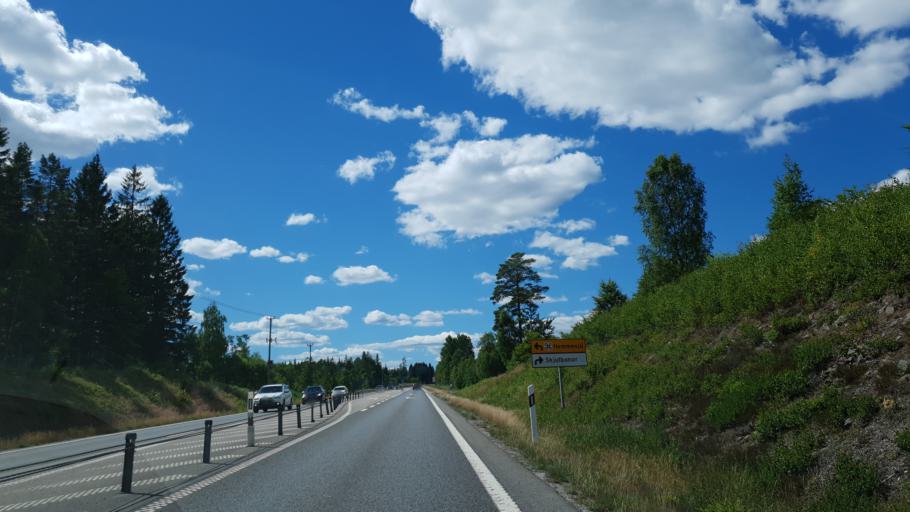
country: SE
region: Kronoberg
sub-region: Vaxjo Kommun
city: Vaexjoe
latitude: 56.8768
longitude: 14.9147
